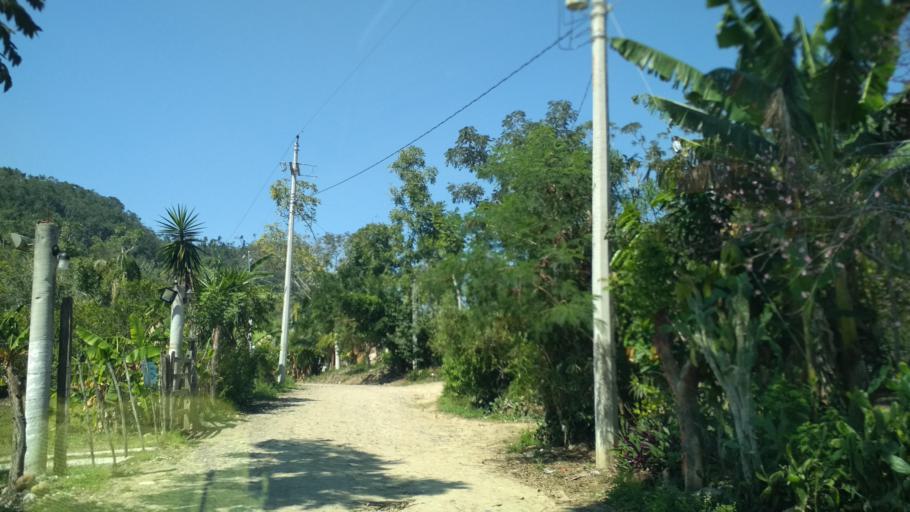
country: MX
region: Veracruz
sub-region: Papantla
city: Polutla
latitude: 20.4833
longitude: -97.2270
